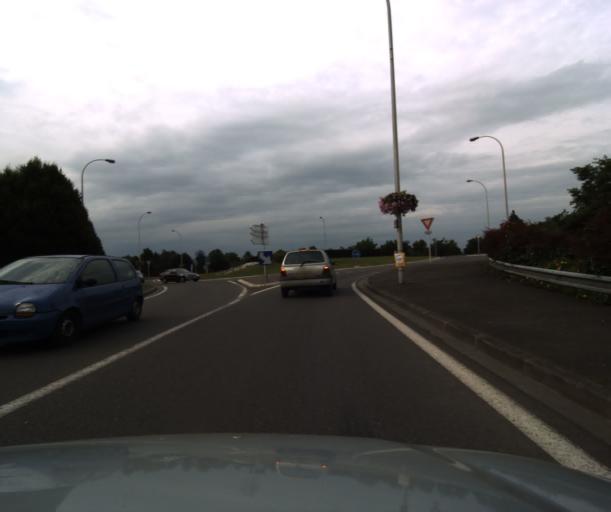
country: FR
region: Midi-Pyrenees
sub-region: Departement des Hautes-Pyrenees
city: Semeac
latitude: 43.2302
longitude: 0.0949
